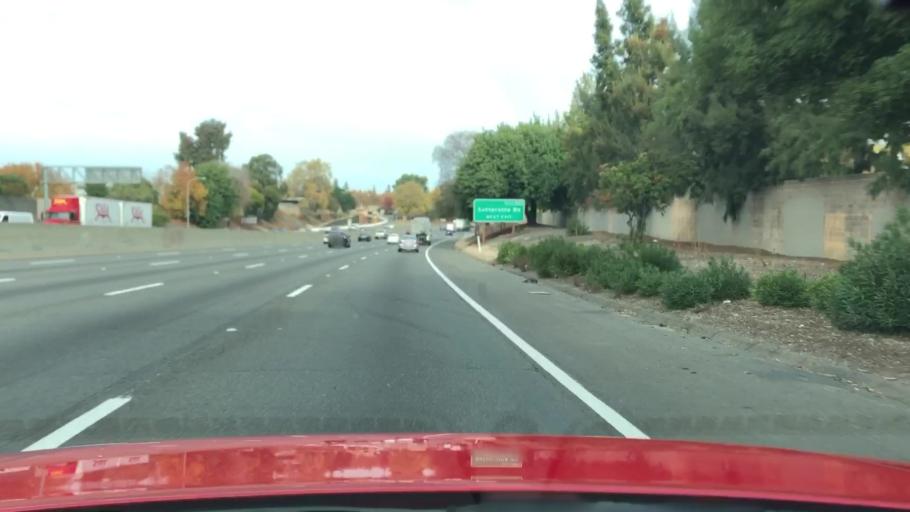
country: US
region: California
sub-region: Sacramento County
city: Parkway
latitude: 38.5354
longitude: -121.4729
